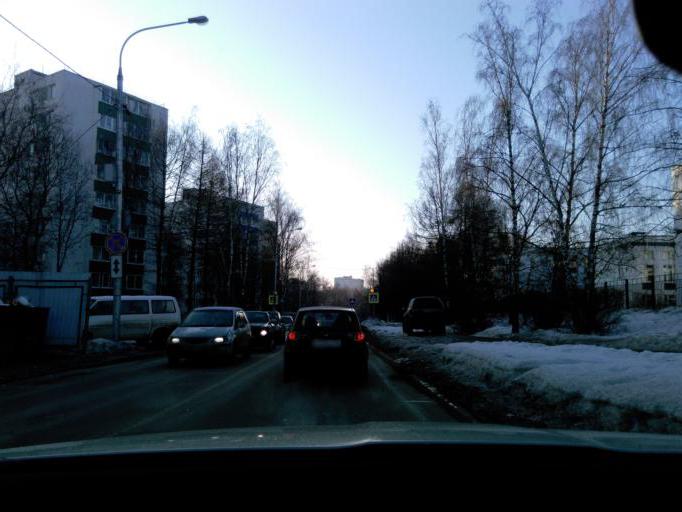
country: RU
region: Moscow
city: Zelenograd
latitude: 55.9962
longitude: 37.2031
